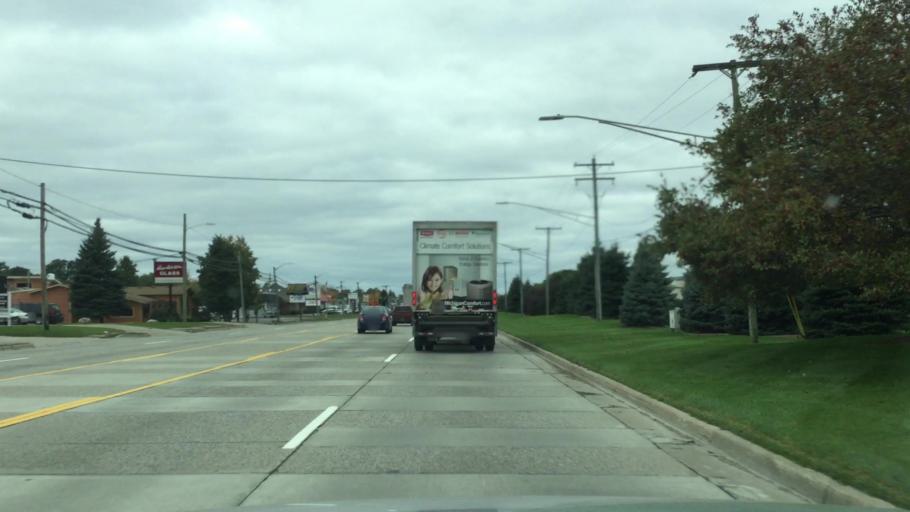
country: US
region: Michigan
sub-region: Oakland County
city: Waterford
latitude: 42.6599
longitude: -83.4090
